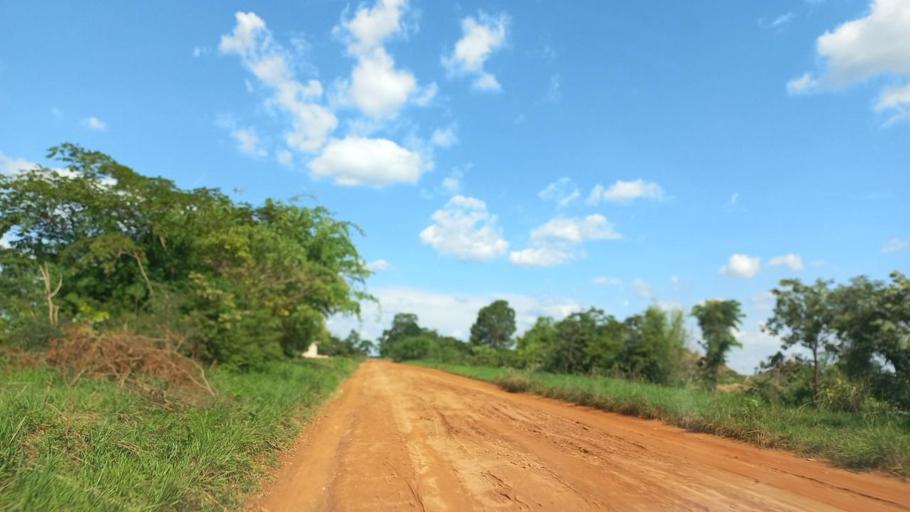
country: ZM
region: Copperbelt
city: Kitwe
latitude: -12.8703
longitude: 28.3496
